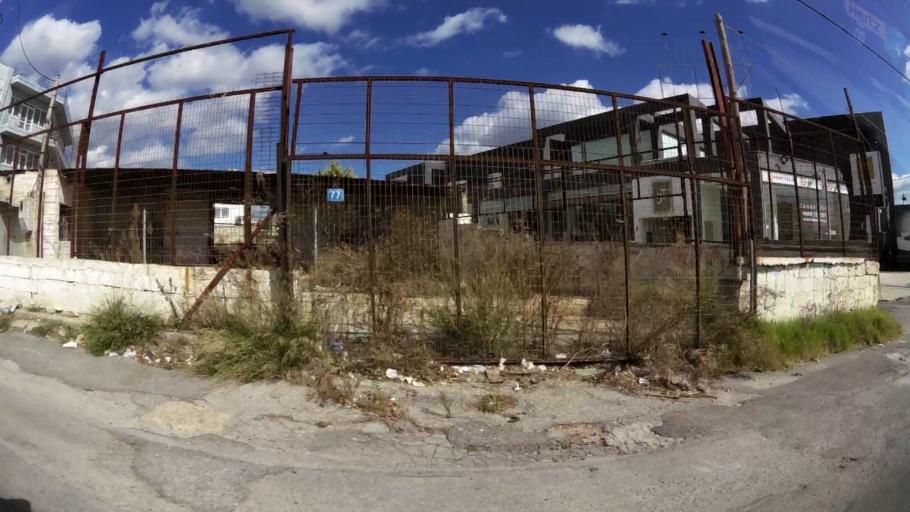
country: GR
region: Attica
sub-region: Nomarchia Anatolikis Attikis
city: Acharnes
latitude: 38.0978
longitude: 23.7474
